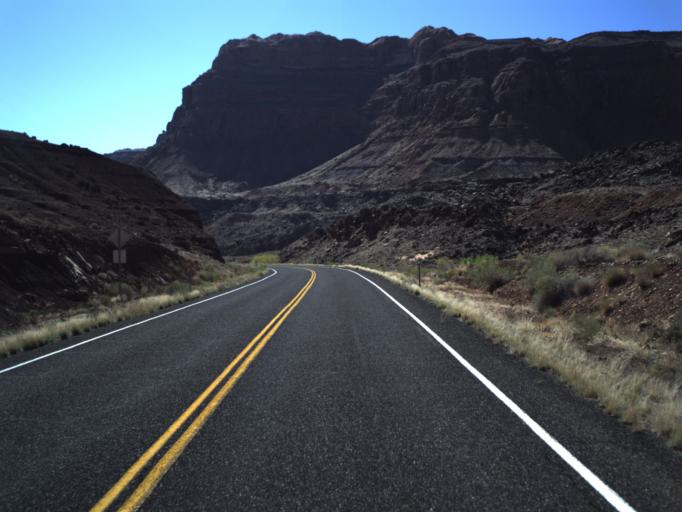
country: US
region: Utah
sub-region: San Juan County
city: Blanding
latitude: 37.9019
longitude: -110.4500
